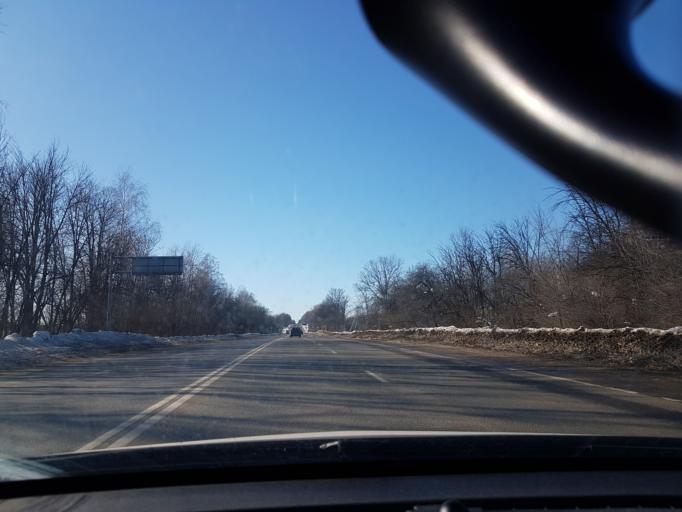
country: RU
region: Moskovskaya
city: Istra
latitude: 55.9075
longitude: 36.8035
